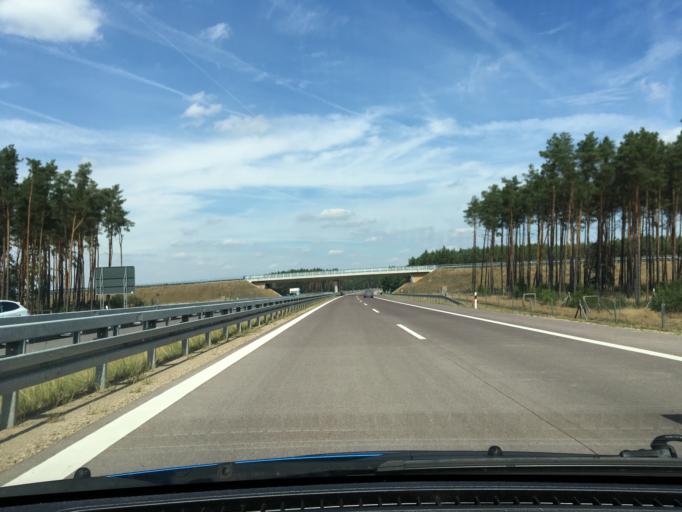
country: DE
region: Mecklenburg-Vorpommern
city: Ludwigslust
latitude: 53.3569
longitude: 11.5157
